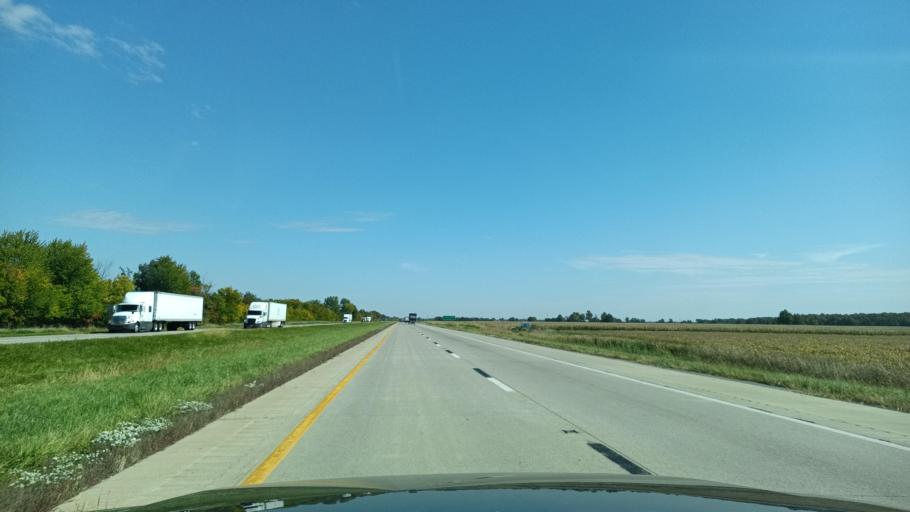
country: US
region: Ohio
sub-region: Paulding County
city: Paulding
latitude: 41.2059
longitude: -84.6433
